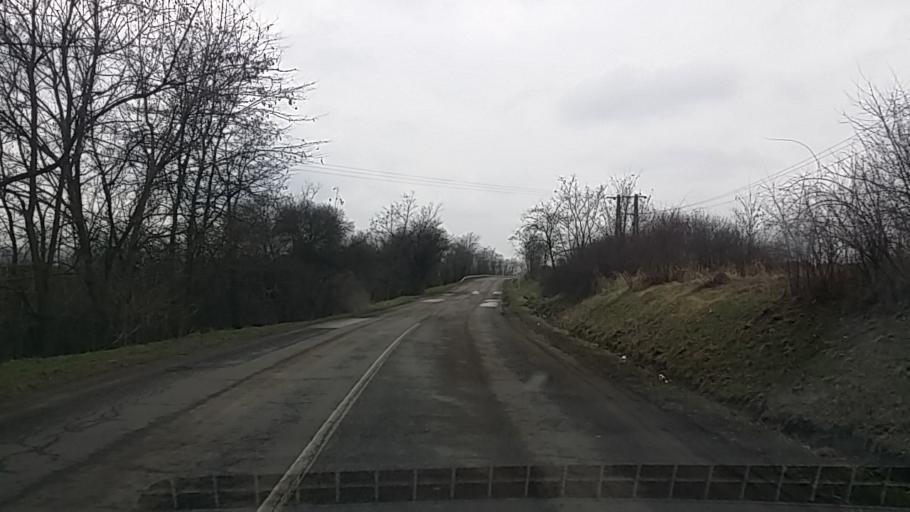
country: HU
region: Borsod-Abauj-Zemplen
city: Mucsony
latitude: 48.2591
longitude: 20.7162
